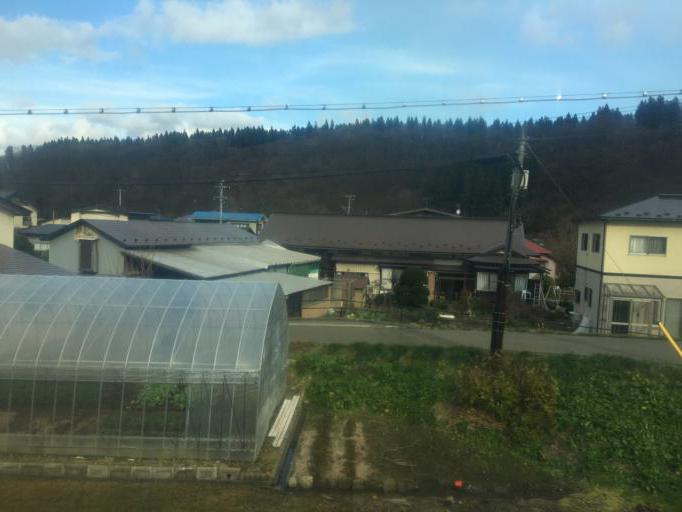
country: JP
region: Akita
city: Noshiromachi
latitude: 40.2034
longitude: 140.1212
